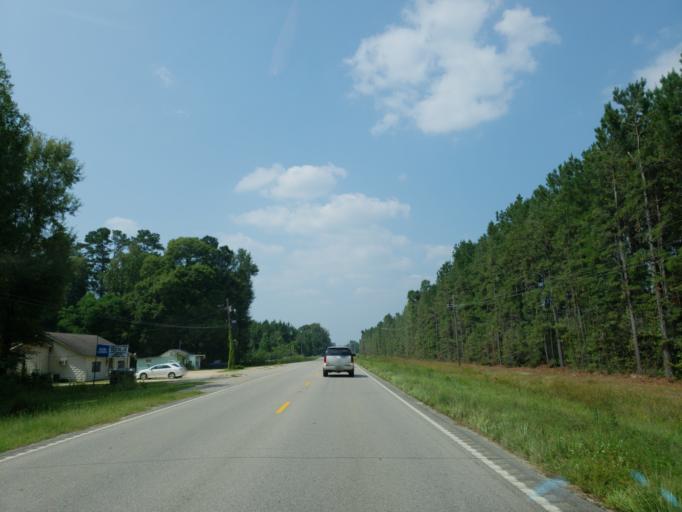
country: US
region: Mississippi
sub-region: Forrest County
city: Glendale
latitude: 31.4285
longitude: -89.2822
